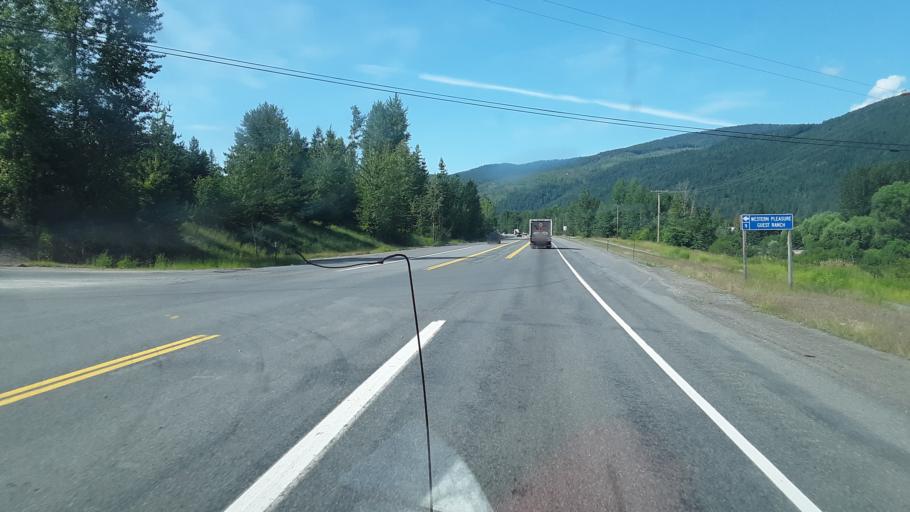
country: US
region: Idaho
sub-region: Bonner County
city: Ponderay
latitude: 48.4009
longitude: -116.5305
